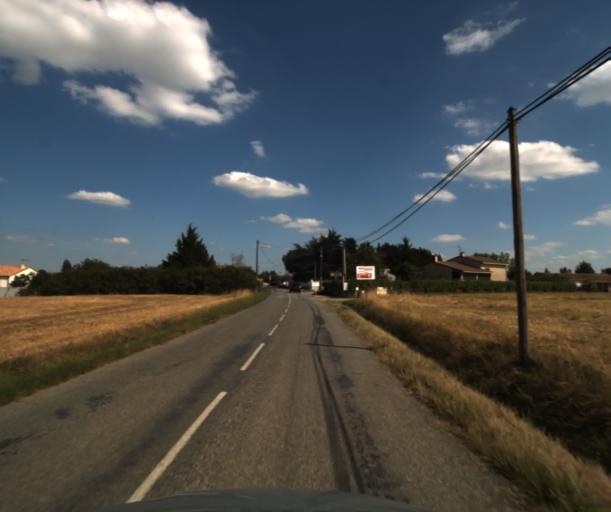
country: FR
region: Midi-Pyrenees
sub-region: Departement de la Haute-Garonne
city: Saint-Lys
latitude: 43.5174
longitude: 1.1694
